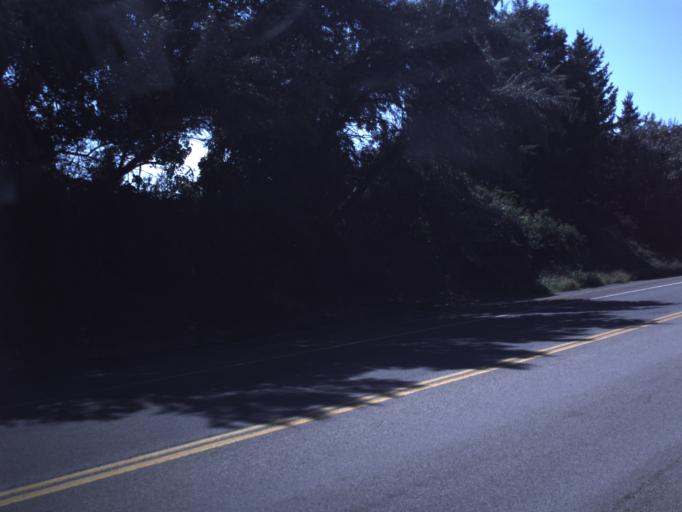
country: US
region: Utah
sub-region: Cache County
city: North Logan
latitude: 41.7437
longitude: -111.7919
